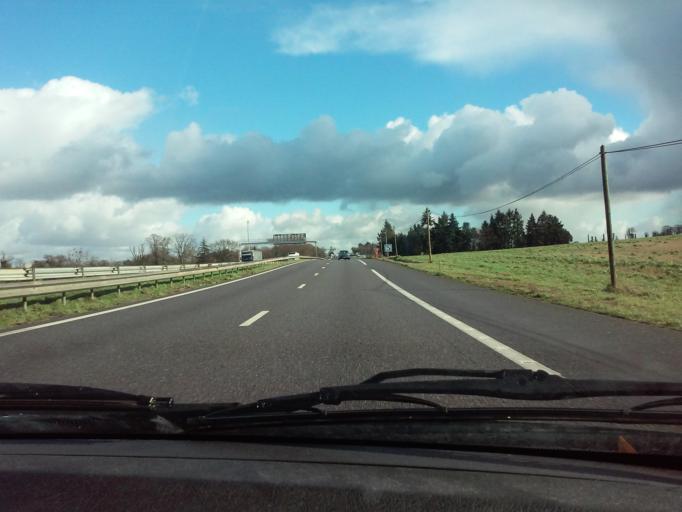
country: FR
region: Brittany
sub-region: Departement d'Ille-et-Vilaine
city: Acigne
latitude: 48.1139
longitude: -1.5552
